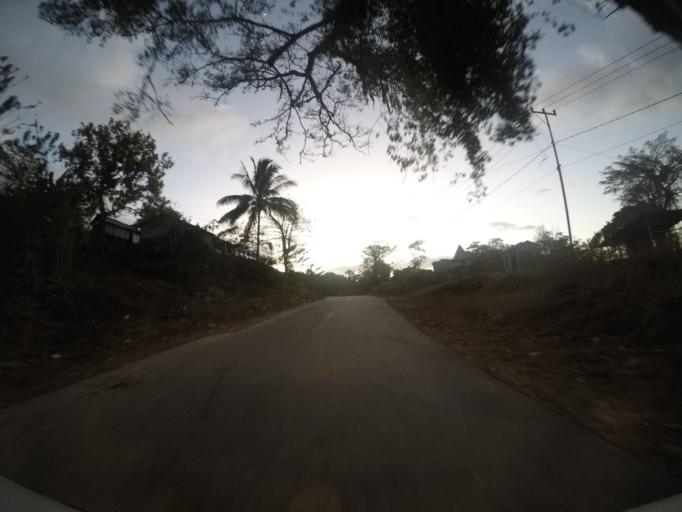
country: TL
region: Lautem
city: Lospalos
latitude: -8.3718
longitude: 127.0278
